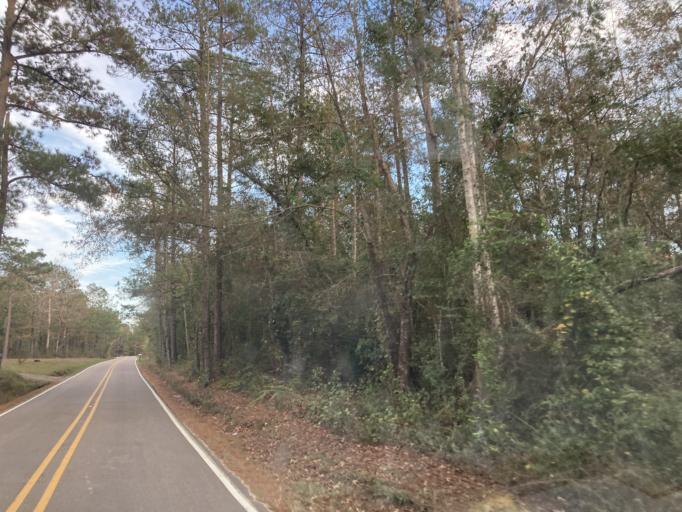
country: US
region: Mississippi
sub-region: Lamar County
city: Purvis
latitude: 31.1825
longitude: -89.3572
